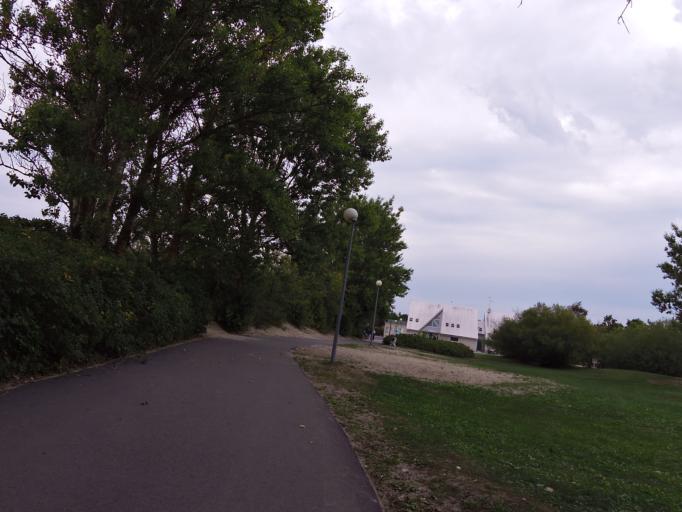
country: EE
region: Harju
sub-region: Tallinna linn
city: Tallinn
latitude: 59.4413
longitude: 24.6839
